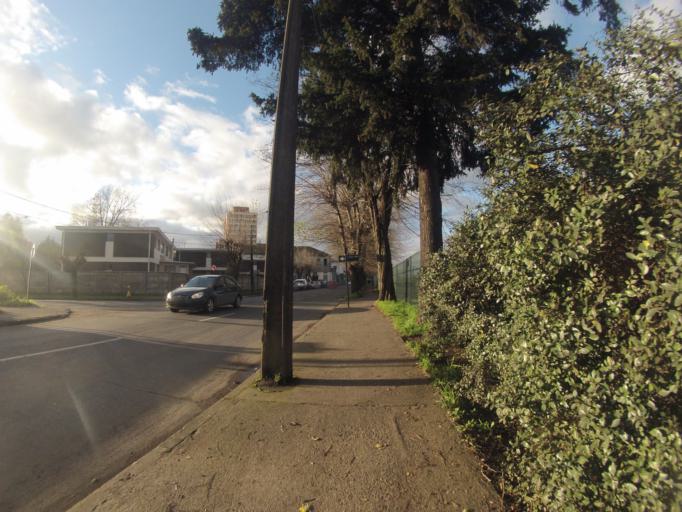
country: CL
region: Araucania
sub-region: Provincia de Cautin
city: Temuco
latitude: -38.7414
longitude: -72.5851
